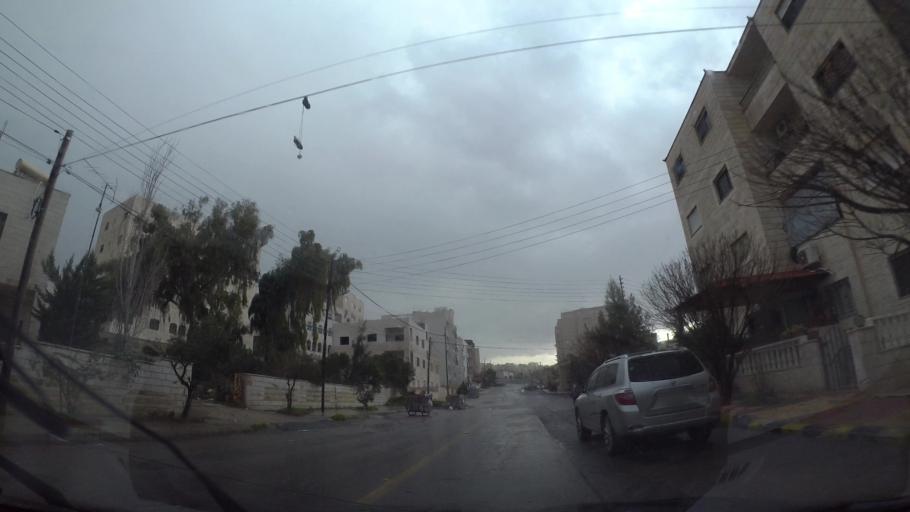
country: JO
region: Amman
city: Amman
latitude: 32.0042
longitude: 35.9585
